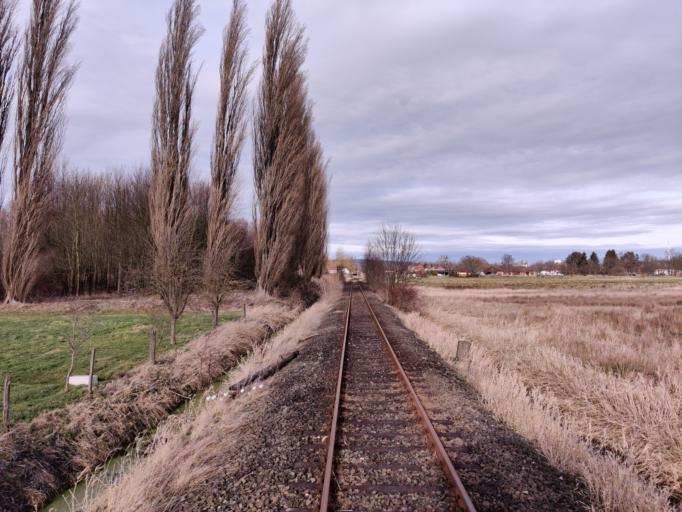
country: DE
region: Lower Saxony
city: Bockenem
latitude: 52.0040
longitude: 10.1214
